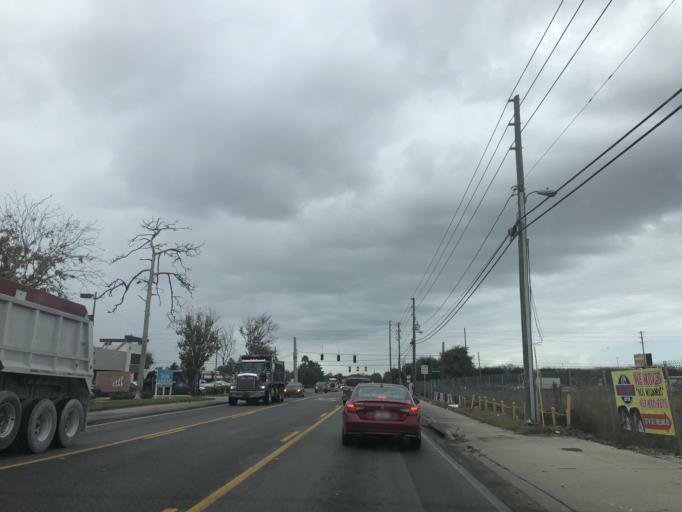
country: US
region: Florida
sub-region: Orange County
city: Southchase
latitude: 28.4214
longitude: -81.4032
